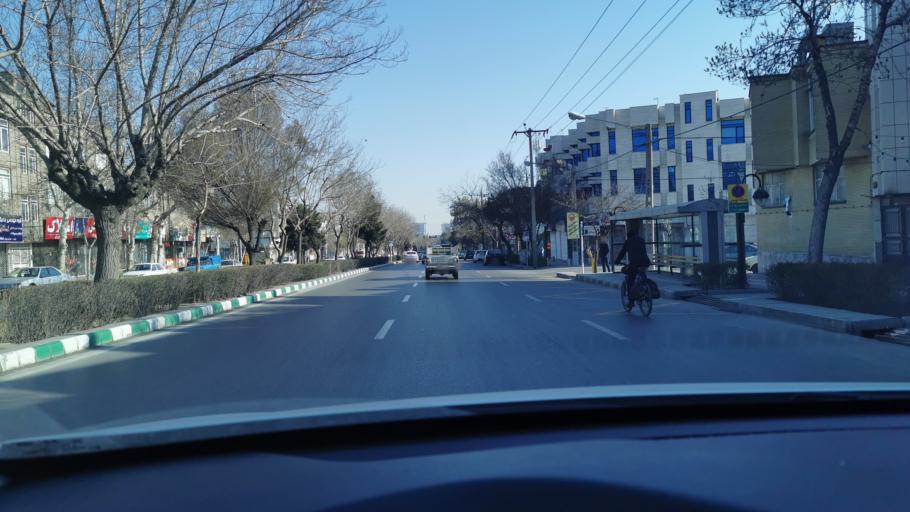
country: IR
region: Razavi Khorasan
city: Mashhad
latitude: 36.2656
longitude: 59.5863
